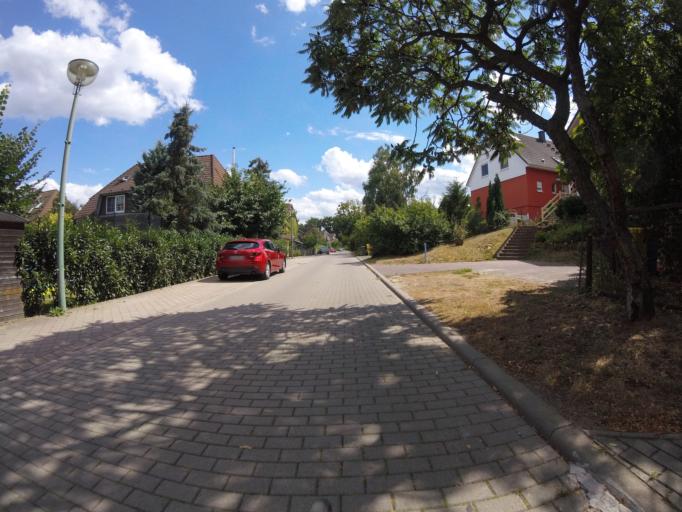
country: DE
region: Brandenburg
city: Werder
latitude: 52.4091
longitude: 12.9879
